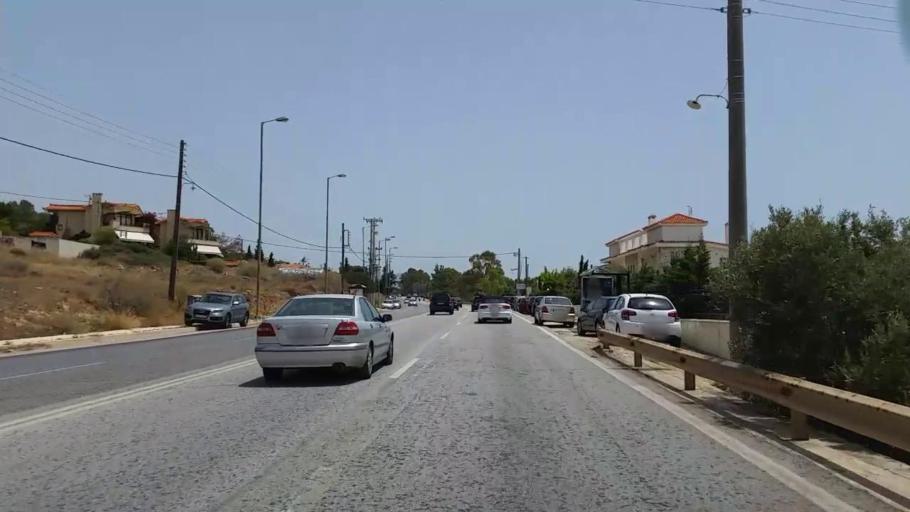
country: GR
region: Attica
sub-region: Nomarchia Anatolikis Attikis
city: Agios Dimitrios Kropias
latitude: 37.8091
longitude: 23.8473
